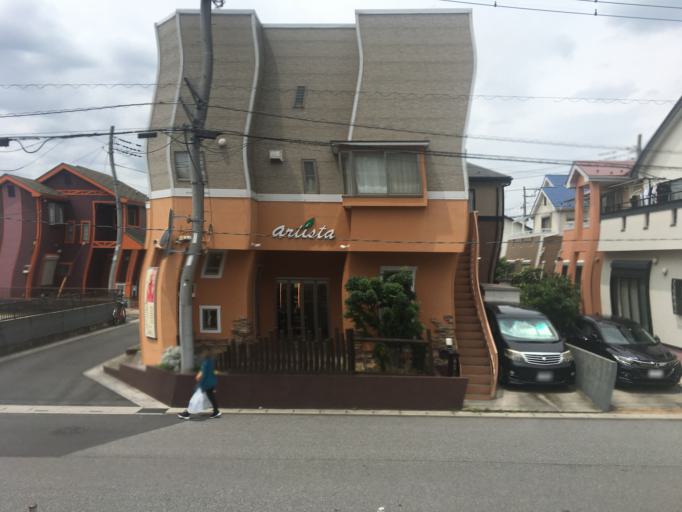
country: JP
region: Saitama
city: Koshigaya
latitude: 35.9219
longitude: 139.7785
